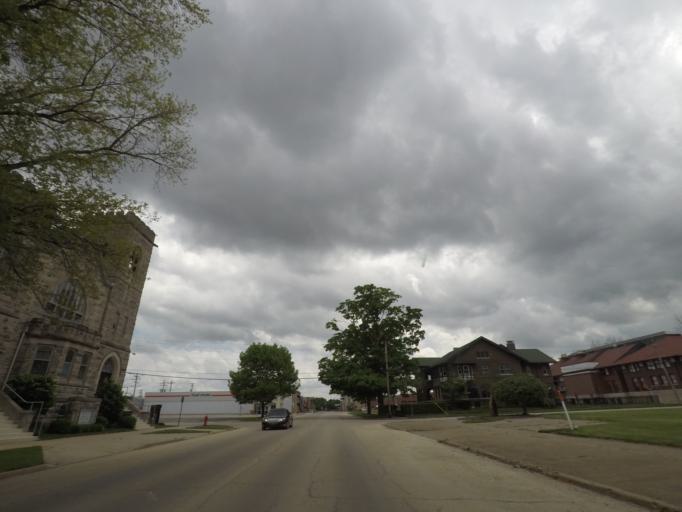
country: US
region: Illinois
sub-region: De Witt County
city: Clinton
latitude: 40.1558
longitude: -88.9605
